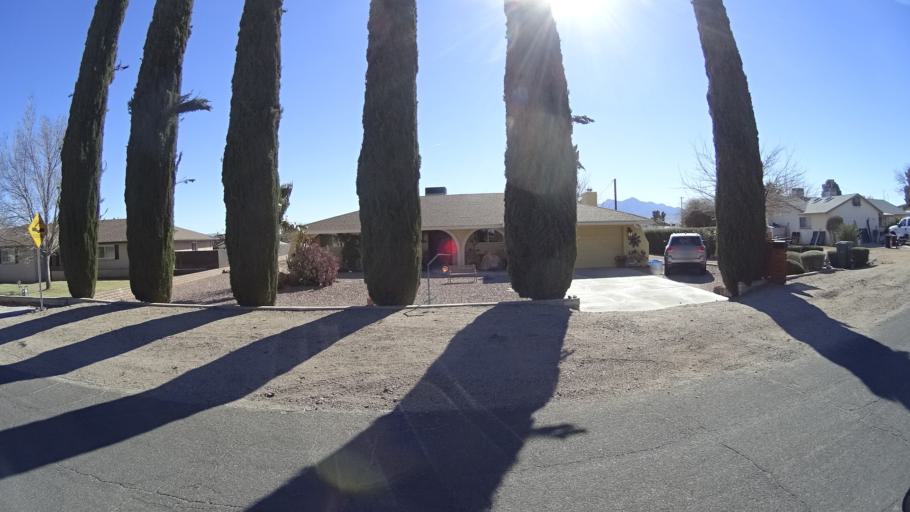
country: US
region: Arizona
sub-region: Mohave County
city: New Kingman-Butler
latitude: 35.2321
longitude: -114.0460
